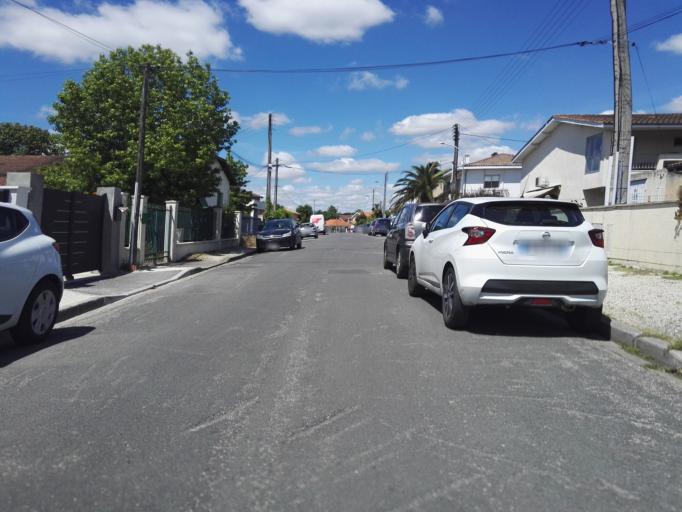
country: FR
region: Aquitaine
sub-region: Departement de la Gironde
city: Begles
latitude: 44.7975
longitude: -0.5606
